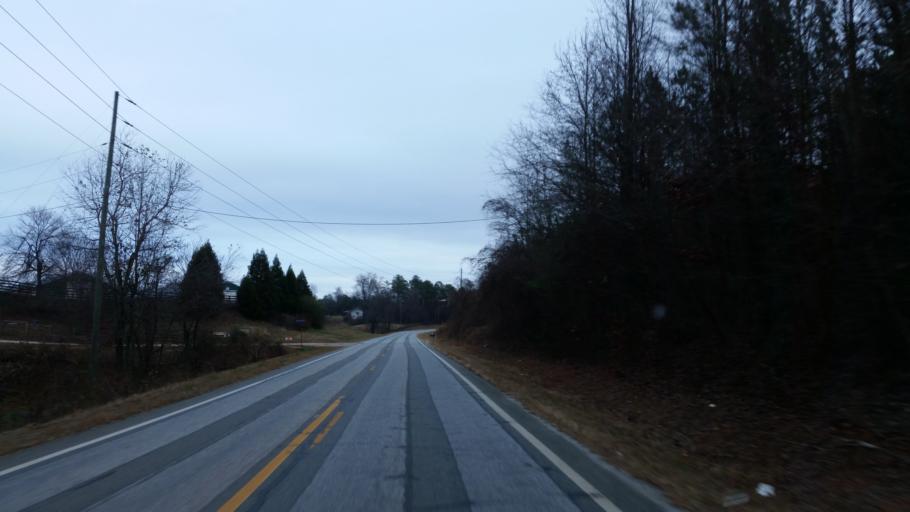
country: US
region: Georgia
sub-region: Dawson County
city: Dawsonville
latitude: 34.5044
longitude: -84.2087
